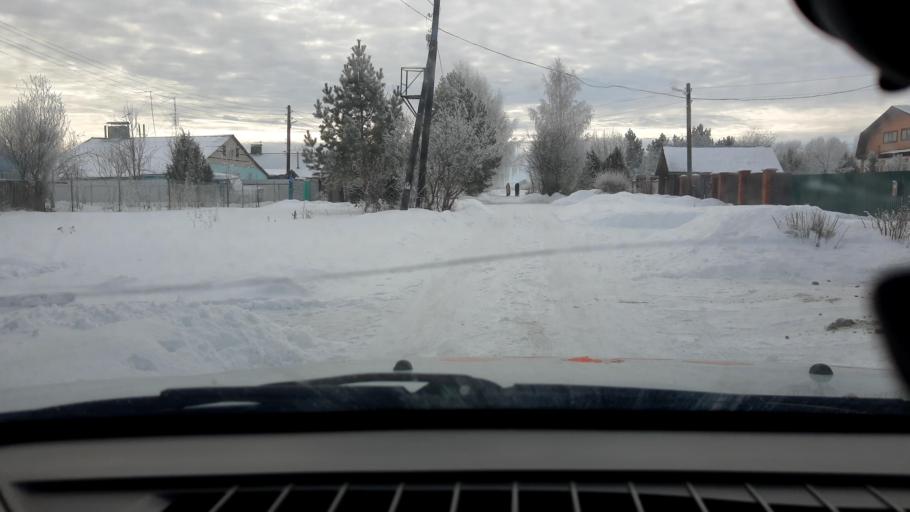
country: RU
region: Nizjnij Novgorod
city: Bogorodsk
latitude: 56.0347
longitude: 43.6191
